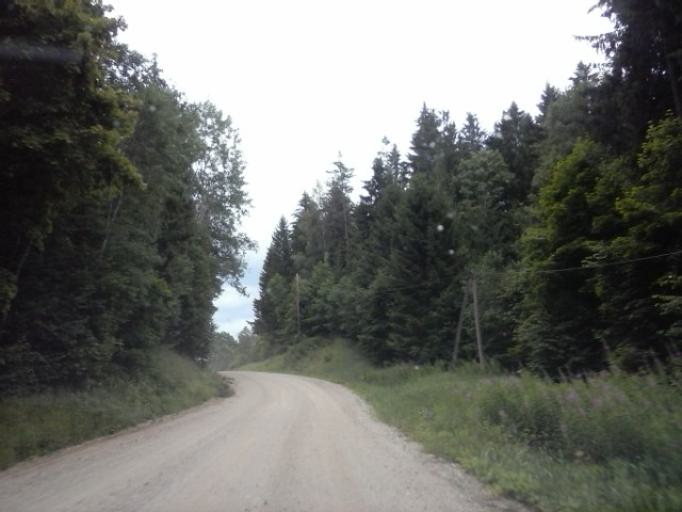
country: EE
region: Vorumaa
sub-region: Voru linn
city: Voru
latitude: 57.7447
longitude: 27.0836
